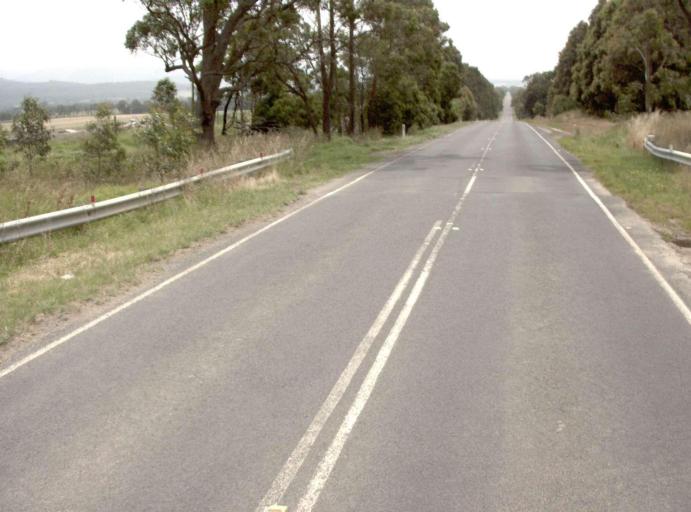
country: AU
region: Victoria
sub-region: Latrobe
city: Traralgon
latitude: -38.5074
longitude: 146.7097
